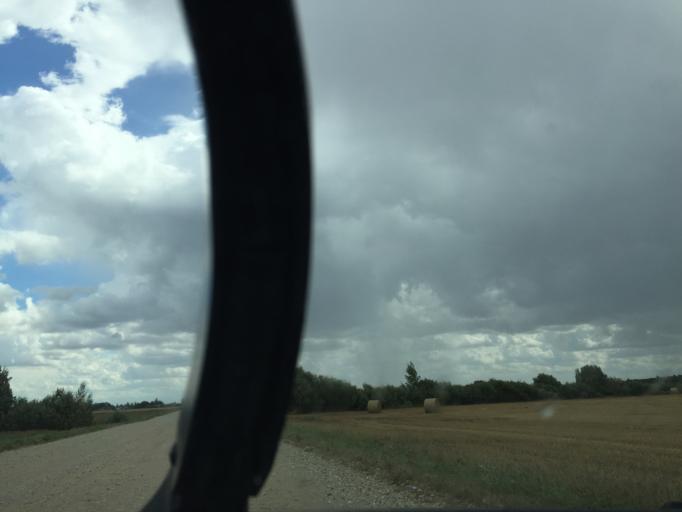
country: LT
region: Siauliu apskritis
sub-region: Joniskis
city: Joniskis
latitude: 56.2822
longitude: 23.7253
